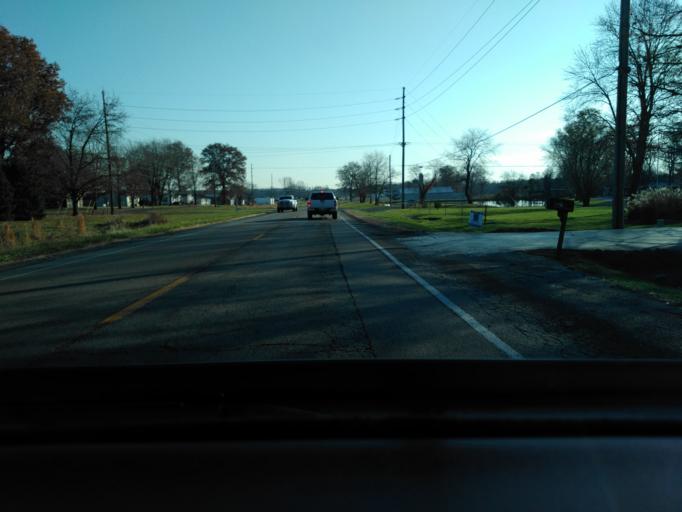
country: US
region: Illinois
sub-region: Madison County
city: Troy
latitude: 38.7175
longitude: -89.8481
